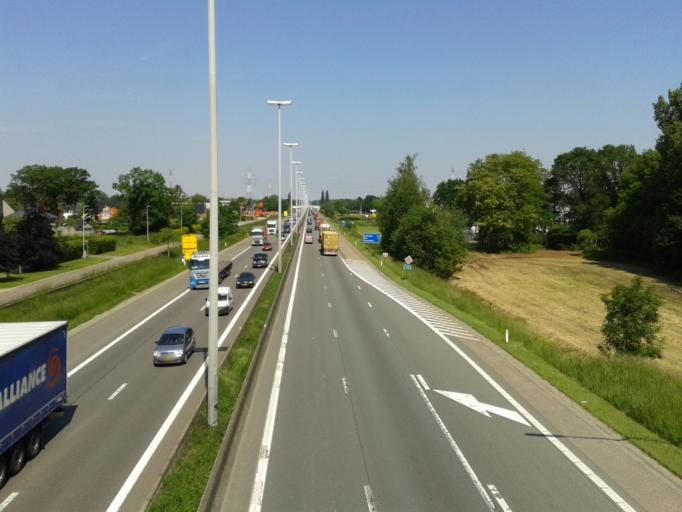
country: BE
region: Flanders
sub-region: Provincie Limburg
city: Beringen
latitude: 51.0461
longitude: 5.1799
